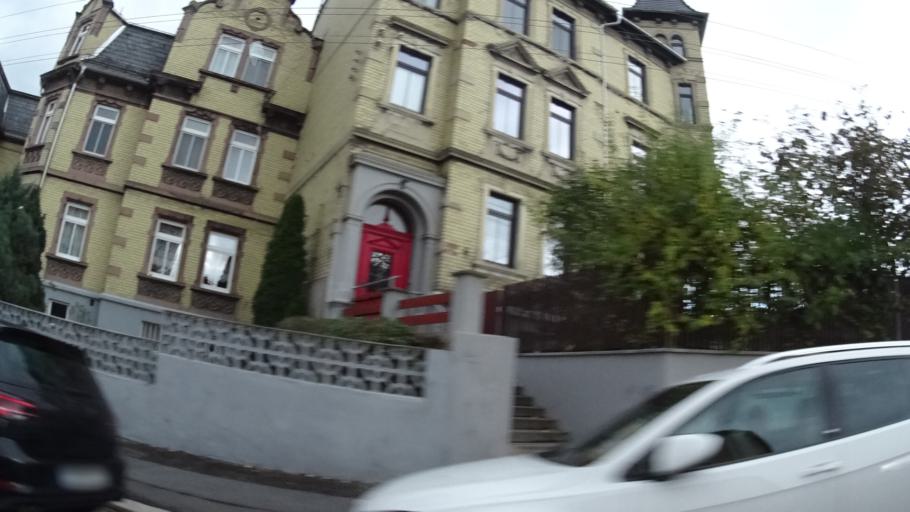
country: DE
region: Thuringia
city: Possneck
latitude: 50.6970
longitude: 11.6039
